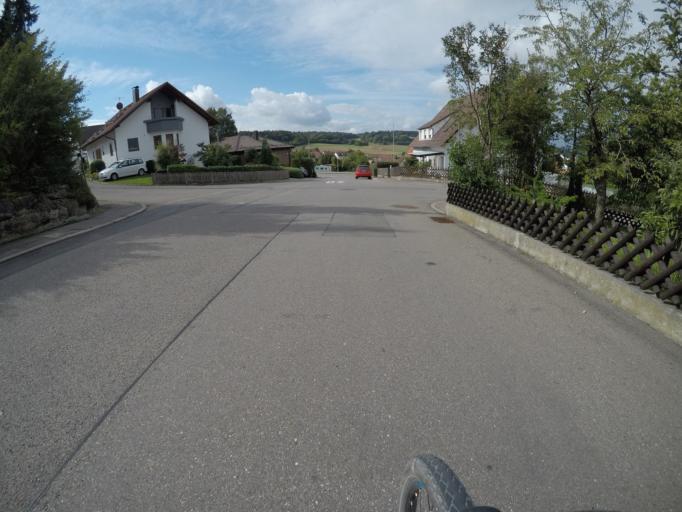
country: DE
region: Baden-Wuerttemberg
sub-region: Karlsruhe Region
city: Althengstett
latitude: 48.7214
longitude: 8.7974
